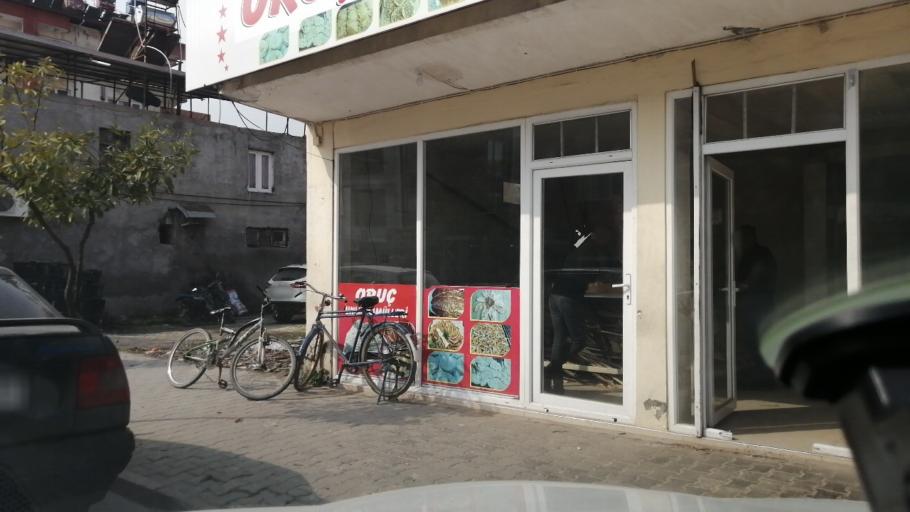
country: TR
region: Hatay
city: Serinyol
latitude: 36.3617
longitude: 36.2124
